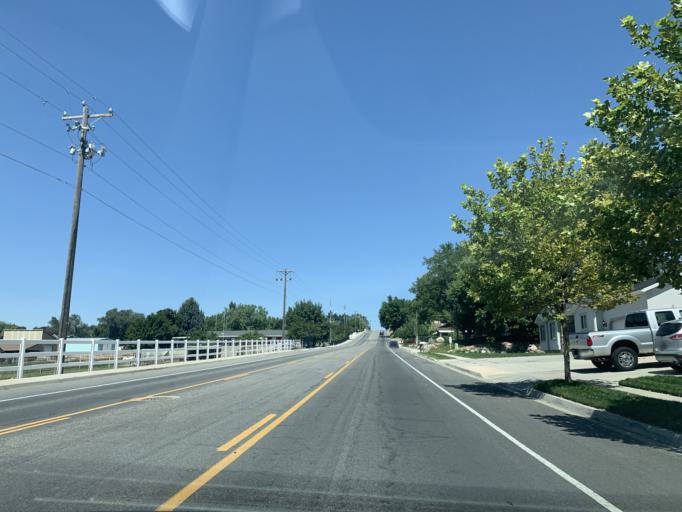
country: US
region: Utah
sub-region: Utah County
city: Lehi
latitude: 40.4019
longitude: -111.8302
